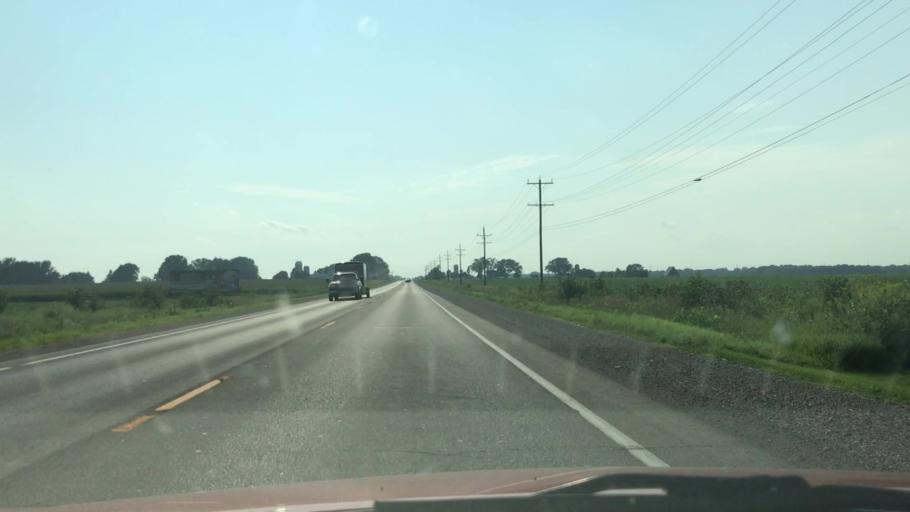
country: US
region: Wisconsin
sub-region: Outagamie County
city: Seymour
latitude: 44.5010
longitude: -88.3041
